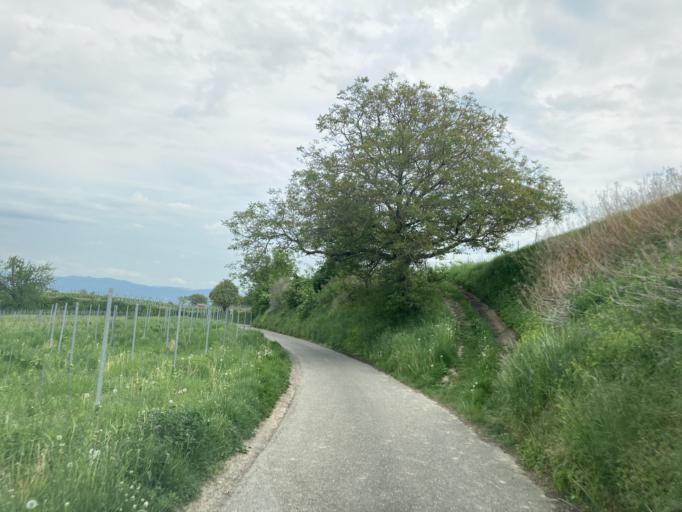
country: DE
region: Baden-Wuerttemberg
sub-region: Freiburg Region
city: Bahlingen
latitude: 48.1113
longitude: 7.7203
